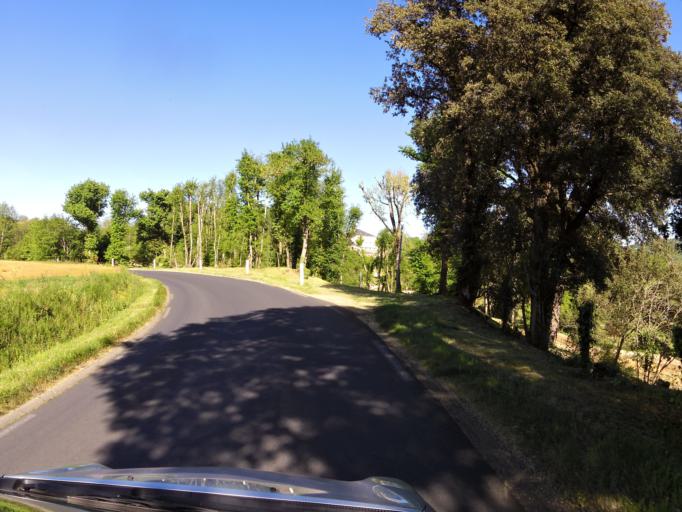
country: FR
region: Aquitaine
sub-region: Departement de la Dordogne
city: Carsac-Aillac
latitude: 44.8314
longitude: 1.2353
